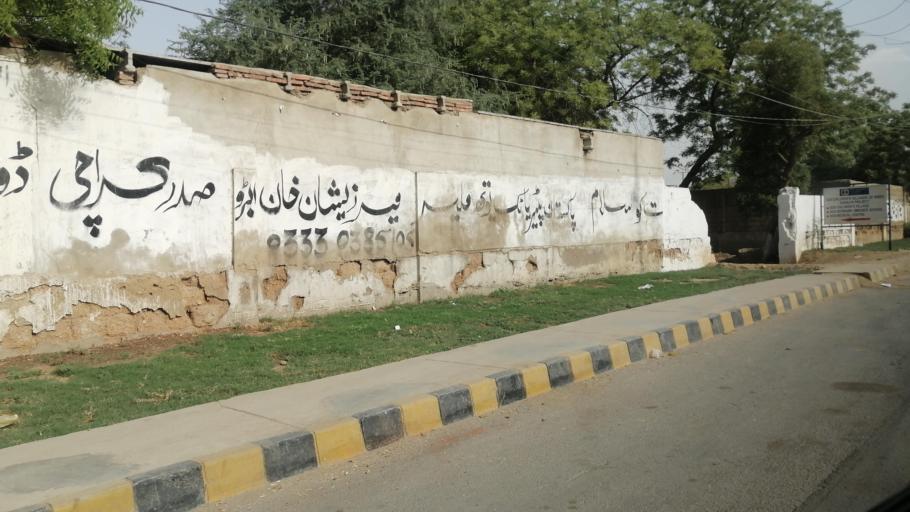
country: PK
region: Sindh
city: Malir Cantonment
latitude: 24.8904
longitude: 67.1772
